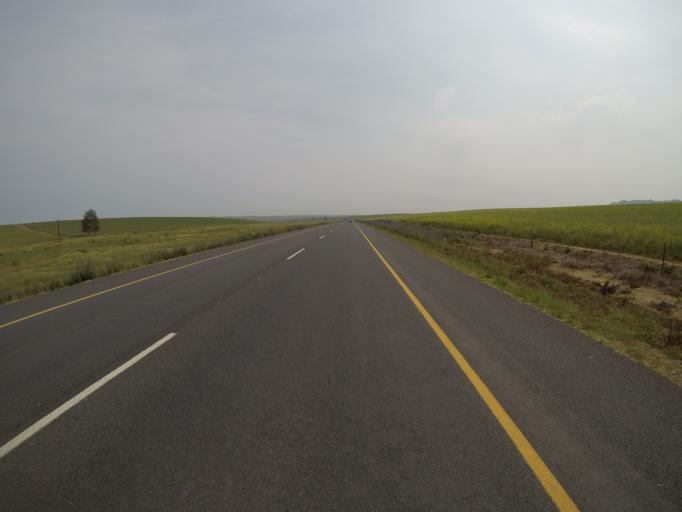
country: ZA
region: Western Cape
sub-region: West Coast District Municipality
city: Malmesbury
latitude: -33.4668
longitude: 18.7906
